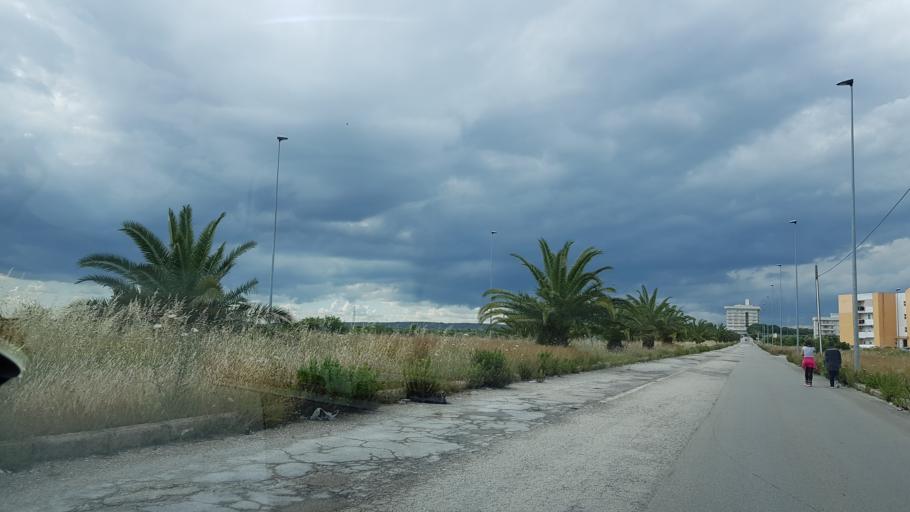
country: IT
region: Apulia
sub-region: Provincia di Taranto
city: Paolo VI
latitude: 40.5308
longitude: 17.2770
